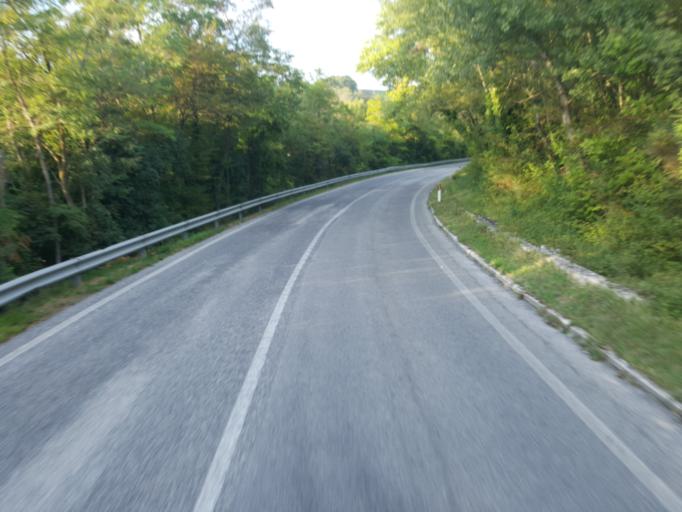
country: IT
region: Umbria
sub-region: Provincia di Perugia
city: Fossato di Vico
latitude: 43.3083
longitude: 12.8242
